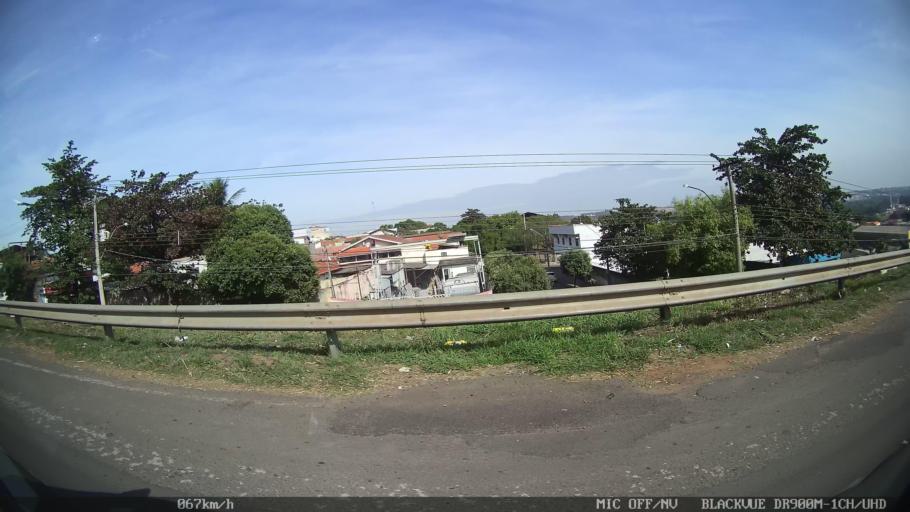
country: BR
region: Sao Paulo
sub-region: Piracicaba
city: Piracicaba
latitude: -22.6928
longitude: -47.6647
